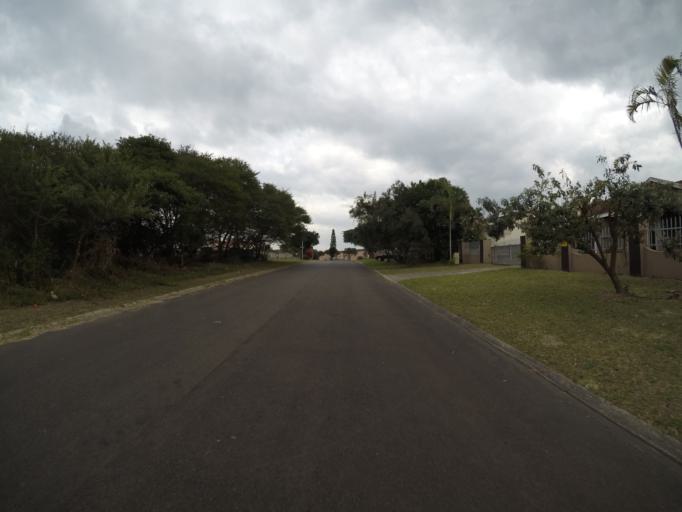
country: ZA
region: KwaZulu-Natal
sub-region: uThungulu District Municipality
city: Richards Bay
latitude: -28.7311
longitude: 32.0535
